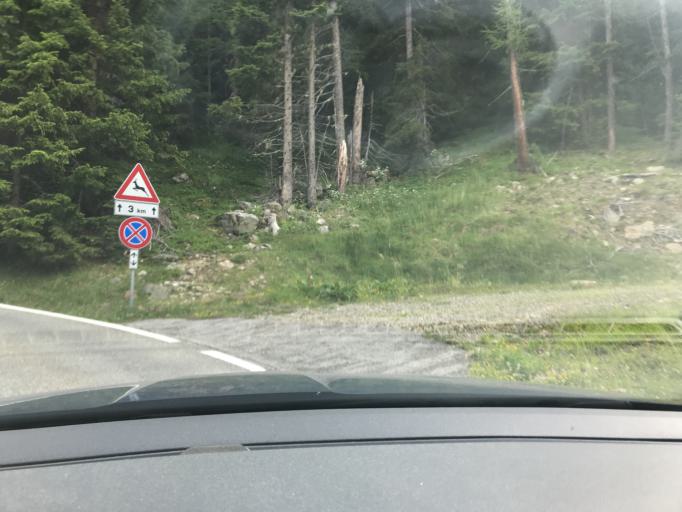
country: IT
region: Trentino-Alto Adige
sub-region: Bolzano
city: San Martino
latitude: 46.8898
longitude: 12.1930
